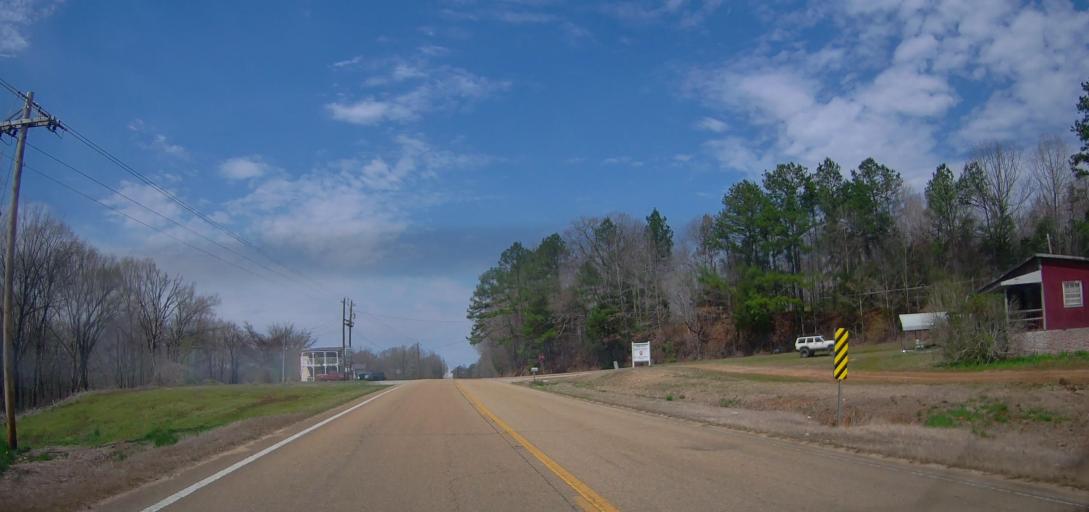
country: US
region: Mississippi
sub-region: Benton County
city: Ashland
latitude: 34.6302
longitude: -89.2707
